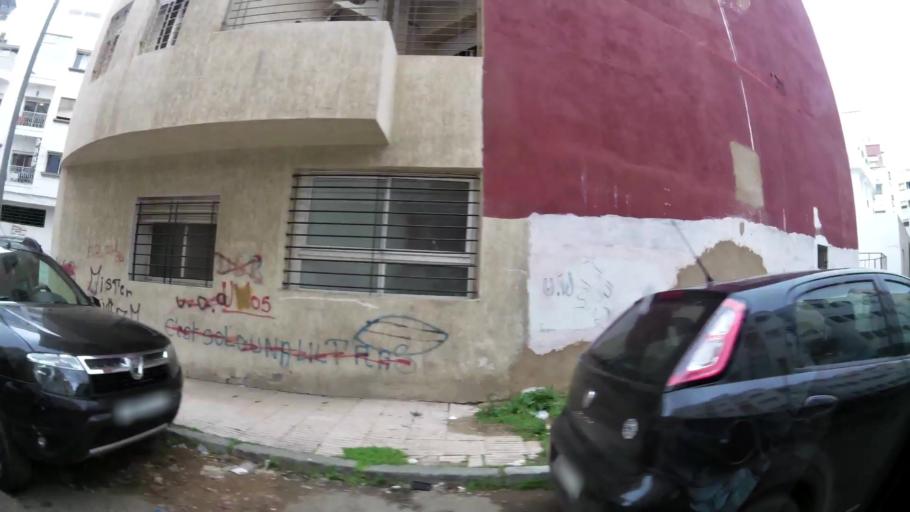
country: MA
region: Grand Casablanca
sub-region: Casablanca
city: Casablanca
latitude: 33.6000
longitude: -7.6469
